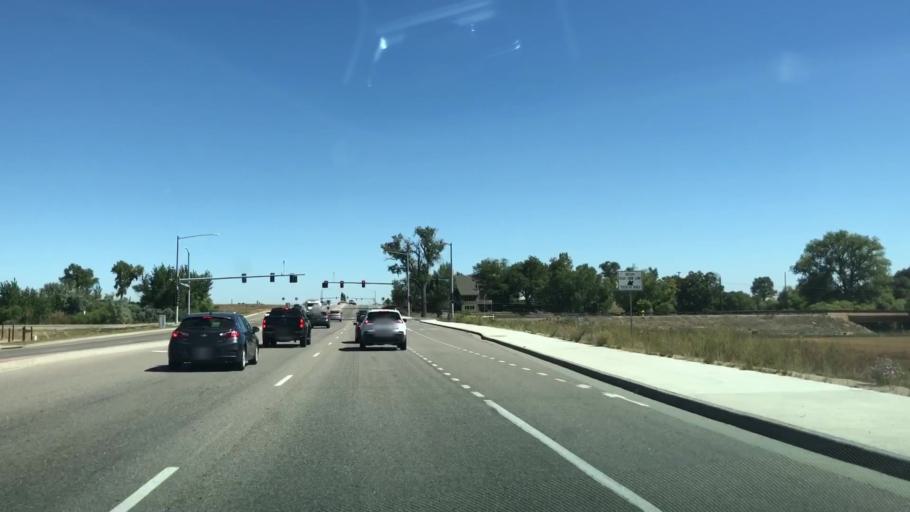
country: US
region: Colorado
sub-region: Weld County
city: Windsor
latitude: 40.5229
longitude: -104.9838
